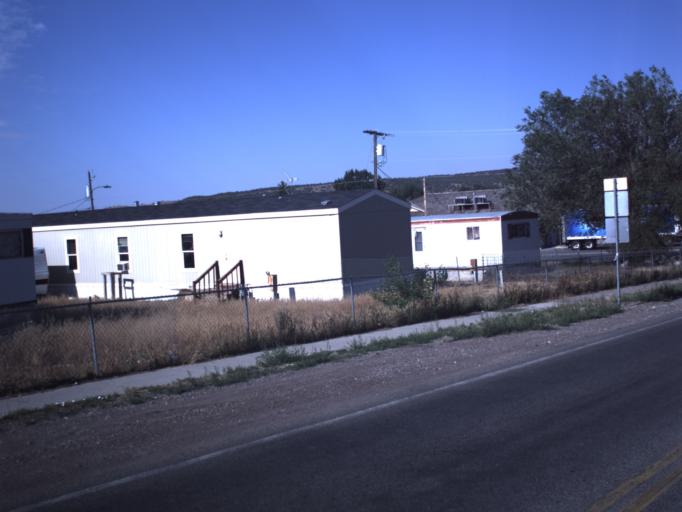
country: US
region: Utah
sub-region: Sanpete County
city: Fairview
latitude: 39.6344
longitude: -111.4385
